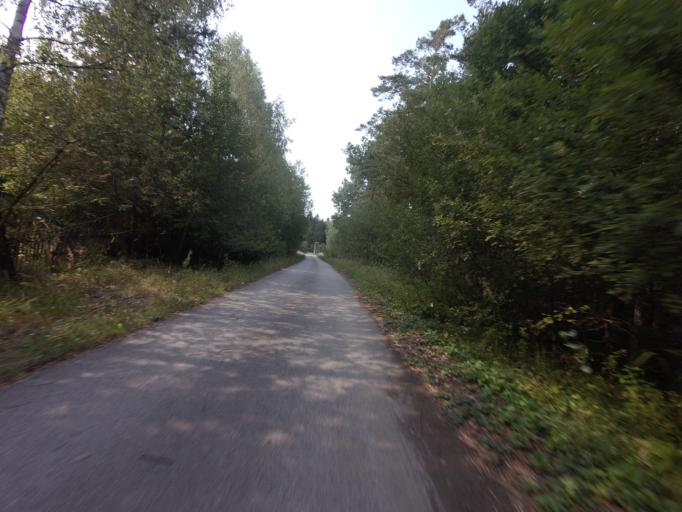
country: CZ
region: Jihocesky
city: Tyn nad Vltavou
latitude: 49.1758
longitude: 14.4402
